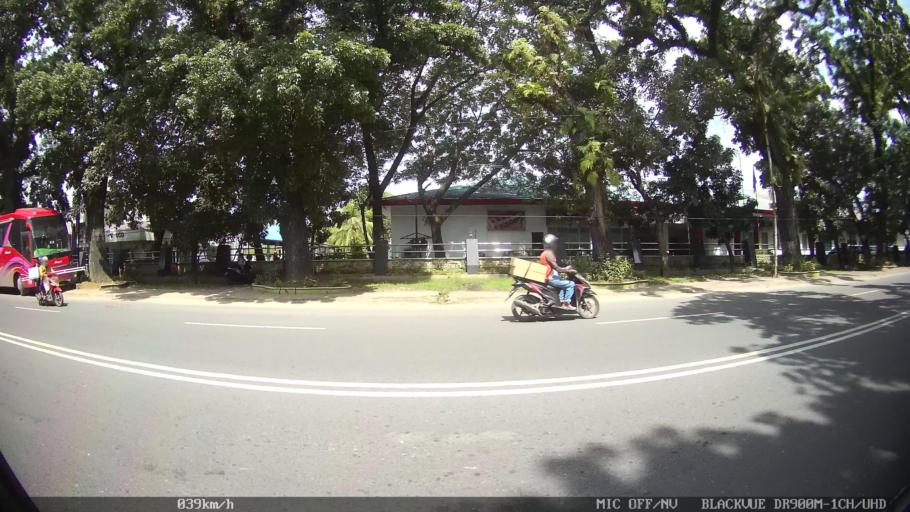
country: ID
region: North Sumatra
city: Medan
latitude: 3.6039
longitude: 98.6735
